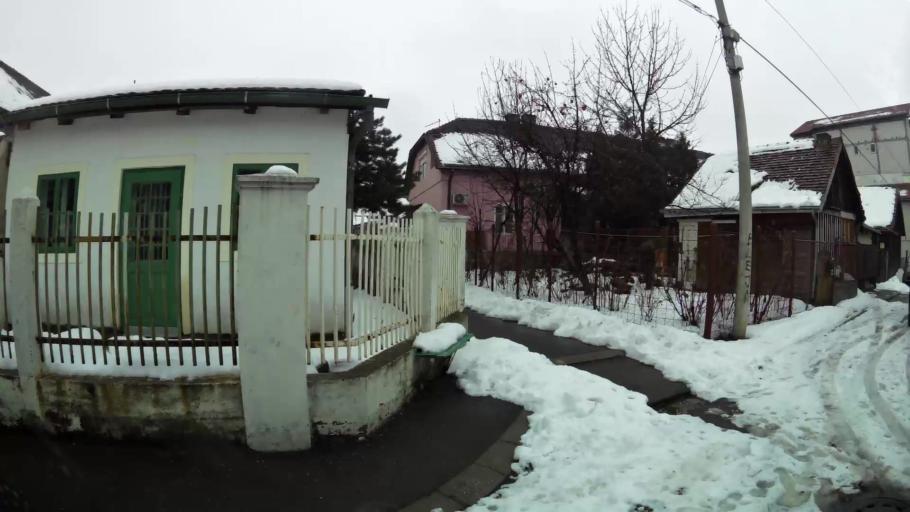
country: RS
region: Central Serbia
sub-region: Belgrade
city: Zemun
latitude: 44.8376
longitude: 20.3727
